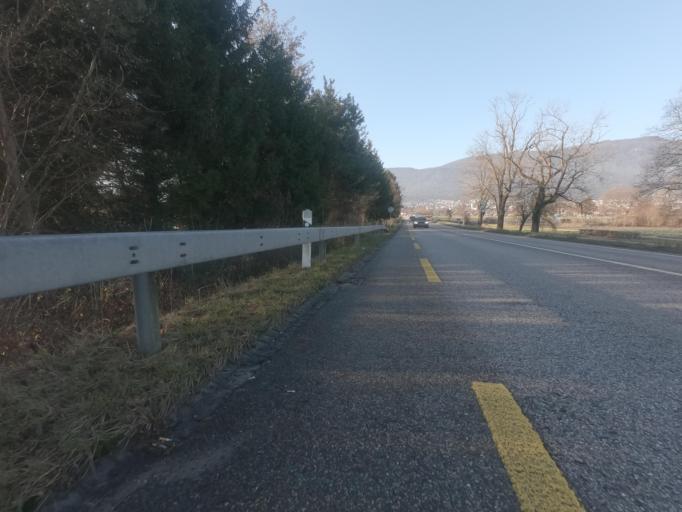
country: CH
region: Bern
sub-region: Seeland District
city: Arch
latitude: 47.1760
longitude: 7.4155
